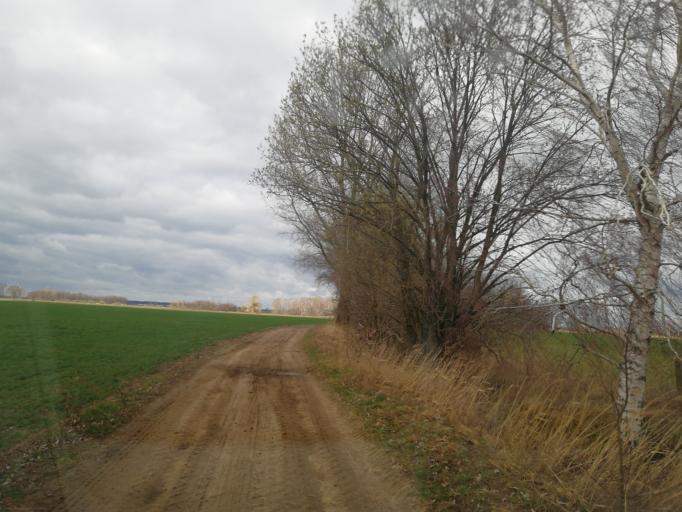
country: DE
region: Brandenburg
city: Schonewalde
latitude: 51.6682
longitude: 13.5623
